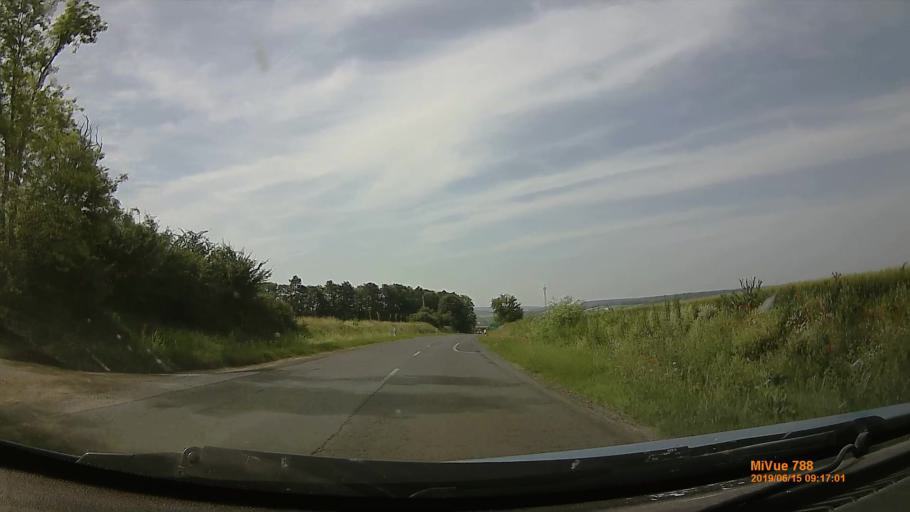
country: HU
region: Tolna
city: Tamasi
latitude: 46.6081
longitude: 18.2074
